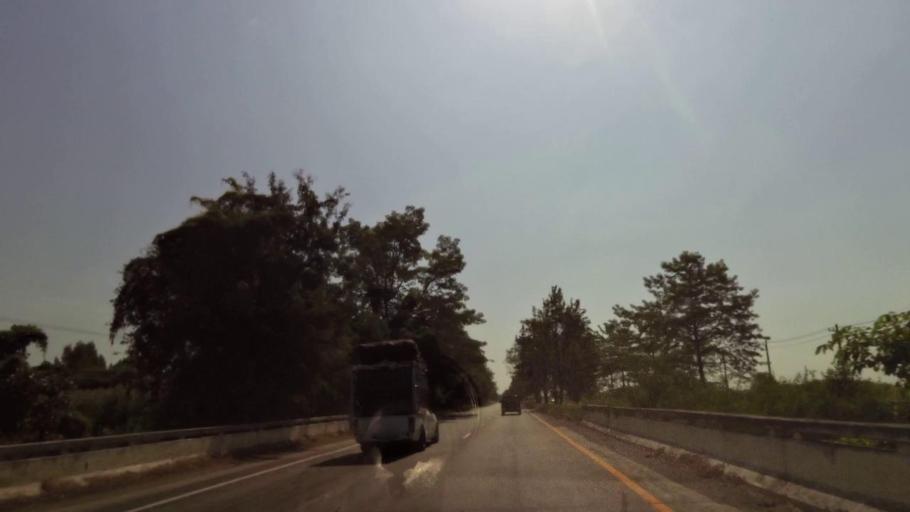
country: TH
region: Nakhon Sawan
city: Kao Liao
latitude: 15.9380
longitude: 100.1134
